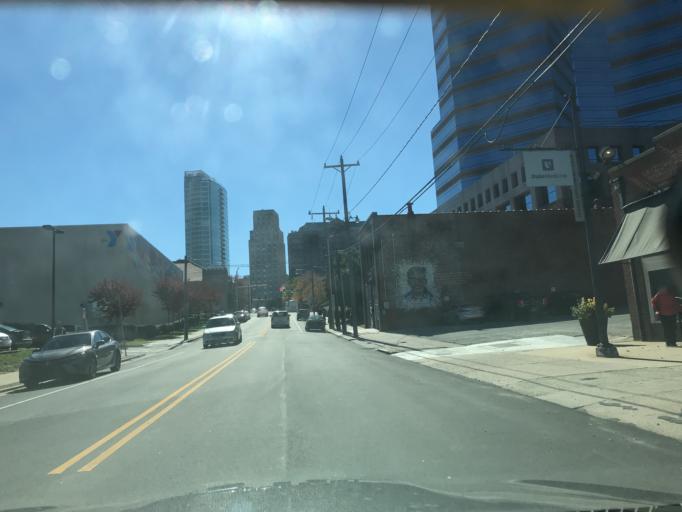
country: US
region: North Carolina
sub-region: Durham County
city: Durham
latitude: 35.9993
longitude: -78.9016
